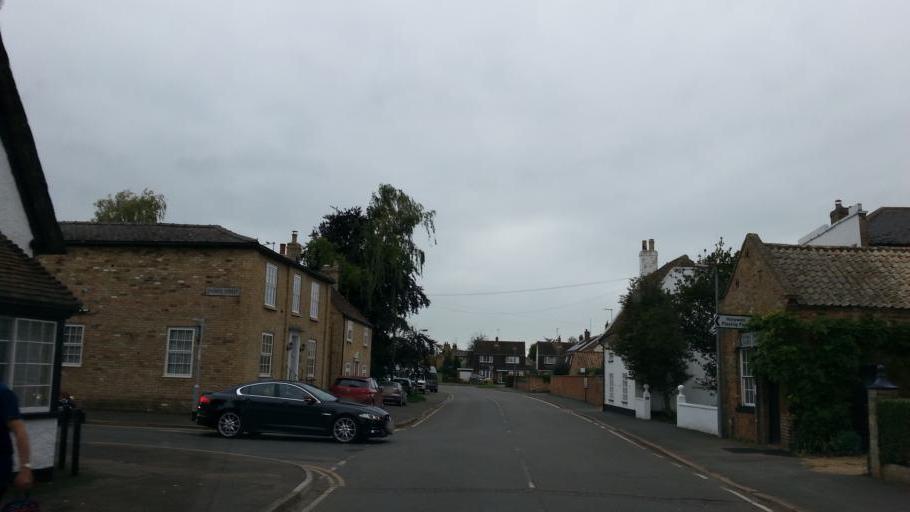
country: GB
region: England
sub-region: Cambridgeshire
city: Needingworth
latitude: 52.3304
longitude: -0.0320
